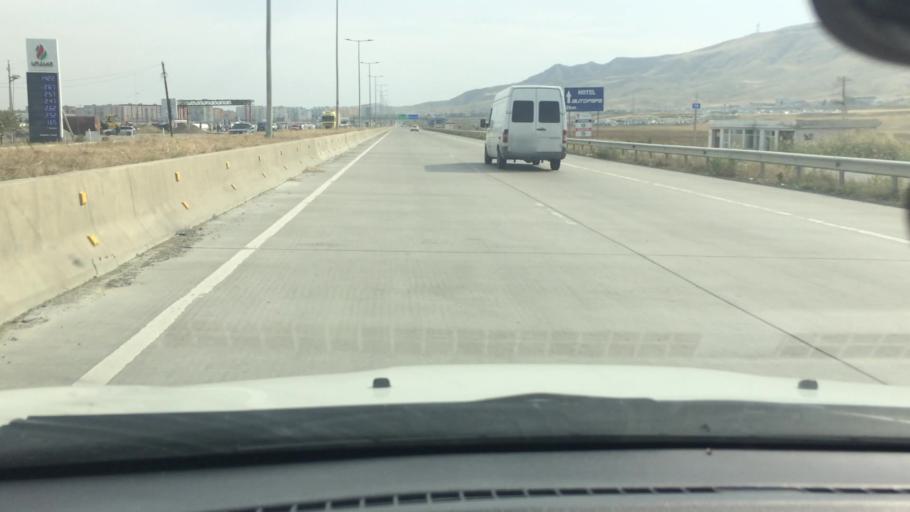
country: GE
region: Kvemo Kartli
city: Rust'avi
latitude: 41.5806
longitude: 44.9535
